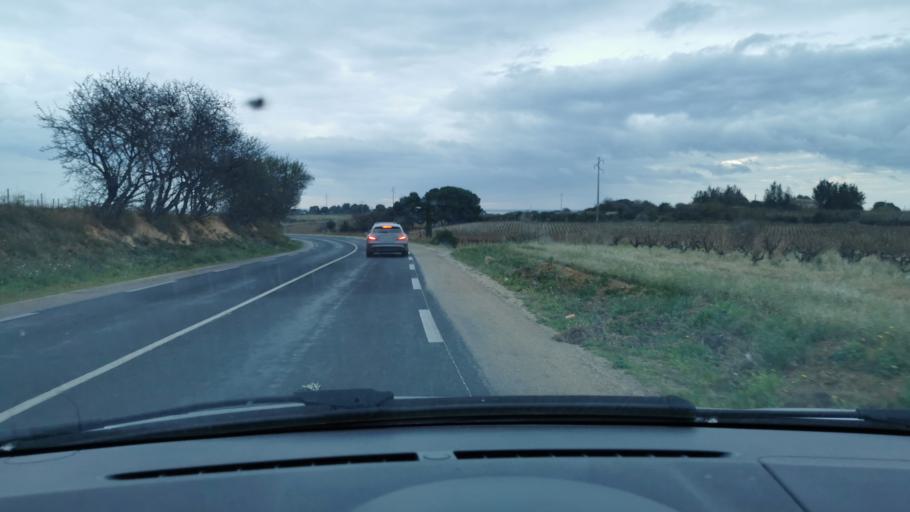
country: FR
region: Languedoc-Roussillon
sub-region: Departement de l'Herault
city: Frontignan
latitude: 43.4484
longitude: 3.7217
